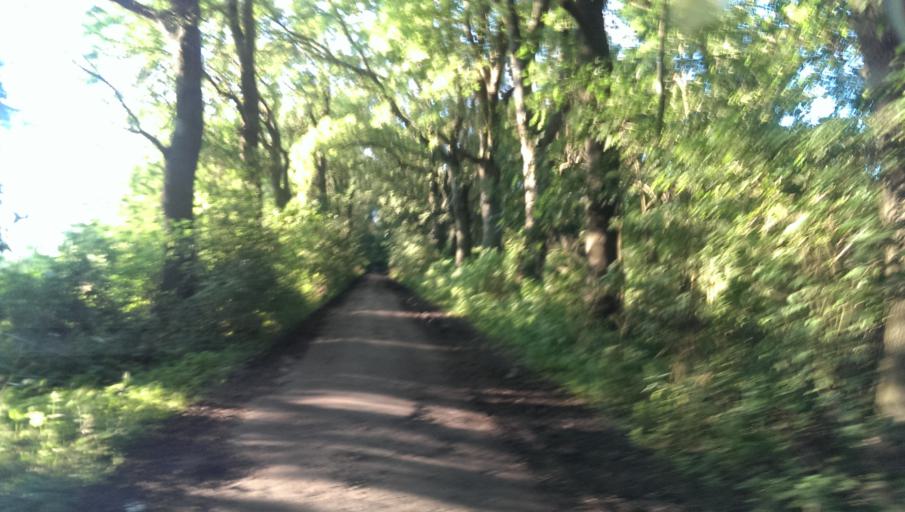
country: DE
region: Brandenburg
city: Trebbin
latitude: 52.2564
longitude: 13.1907
